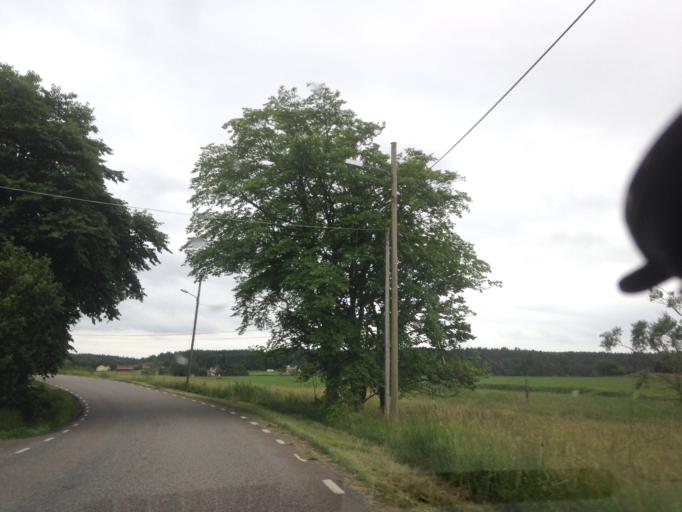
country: SE
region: Vaestra Goetaland
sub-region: Kungalvs Kommun
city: Kode
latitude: 57.8389
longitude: 11.7934
